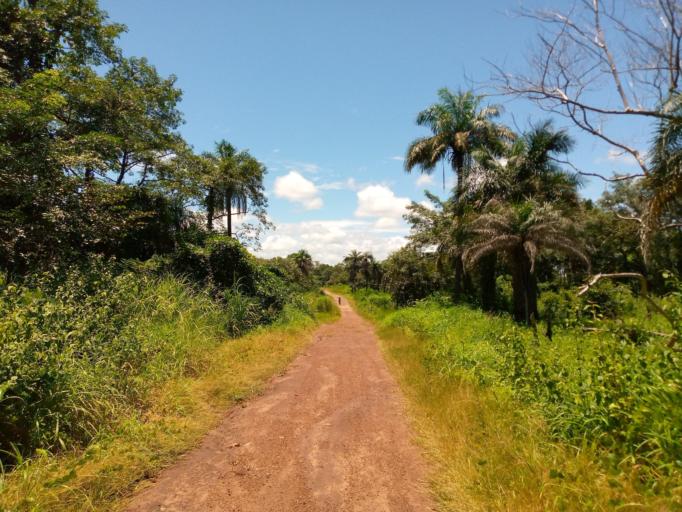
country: SL
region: Northern Province
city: Binkolo
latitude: 9.1058
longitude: -12.1398
